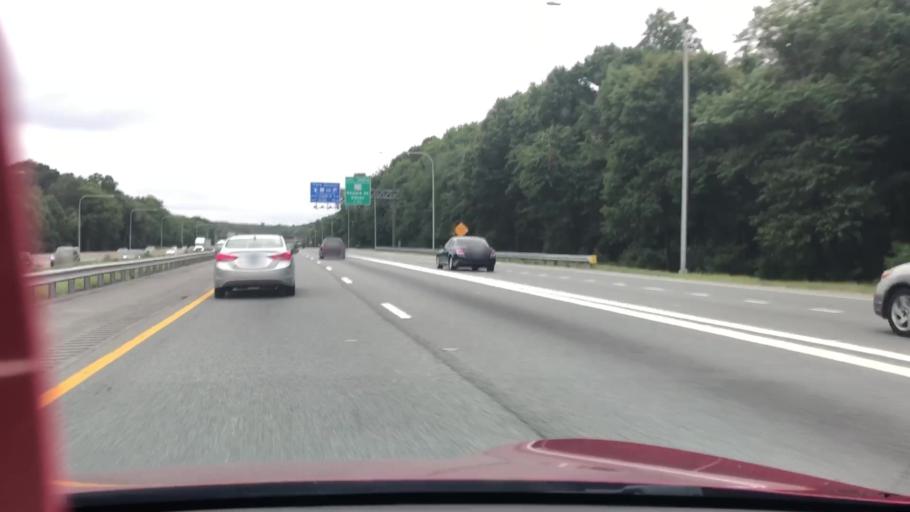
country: US
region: Delaware
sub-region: New Castle County
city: Glasgow
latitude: 39.6426
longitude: -75.7708
